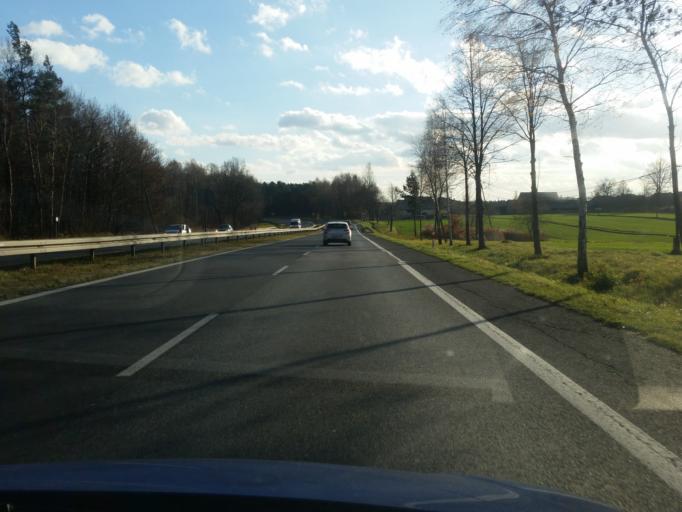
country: PL
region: Silesian Voivodeship
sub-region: Powiat myszkowski
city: Kozieglowy
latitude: 50.5444
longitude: 19.1806
